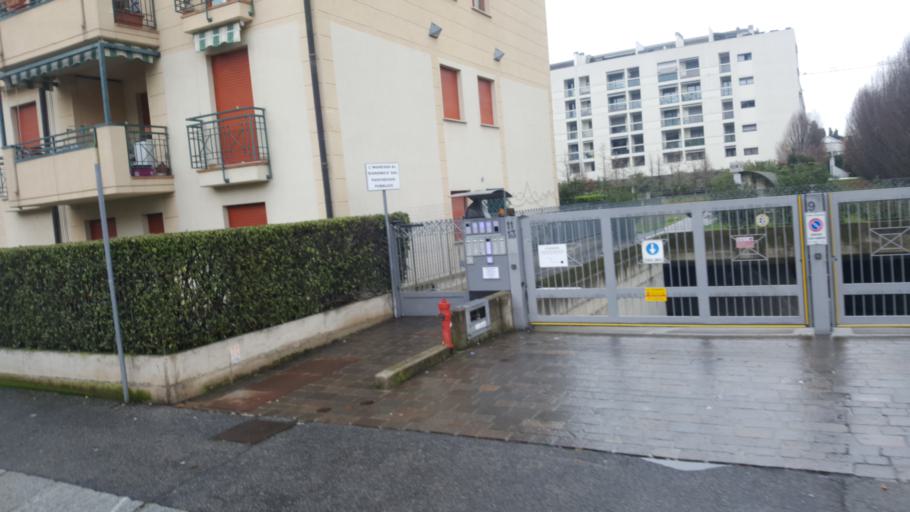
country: IT
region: Lombardy
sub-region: Provincia di Bergamo
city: Bergamo
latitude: 45.6973
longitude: 9.6868
